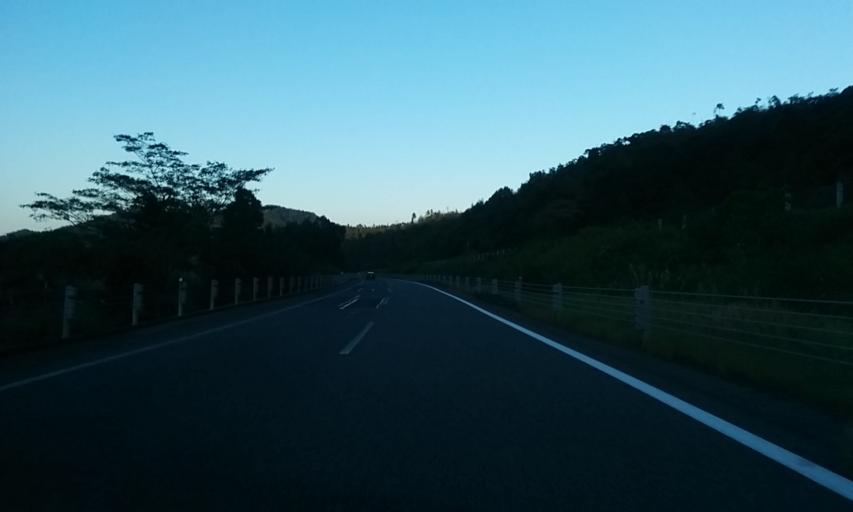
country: JP
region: Kyoto
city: Fukuchiyama
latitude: 35.2225
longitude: 135.1825
